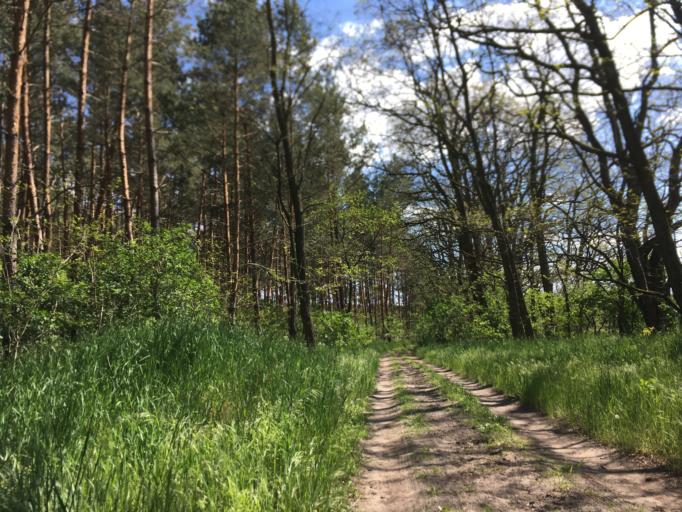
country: DE
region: Brandenburg
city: Rudnitz
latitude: 52.7154
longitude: 13.6574
